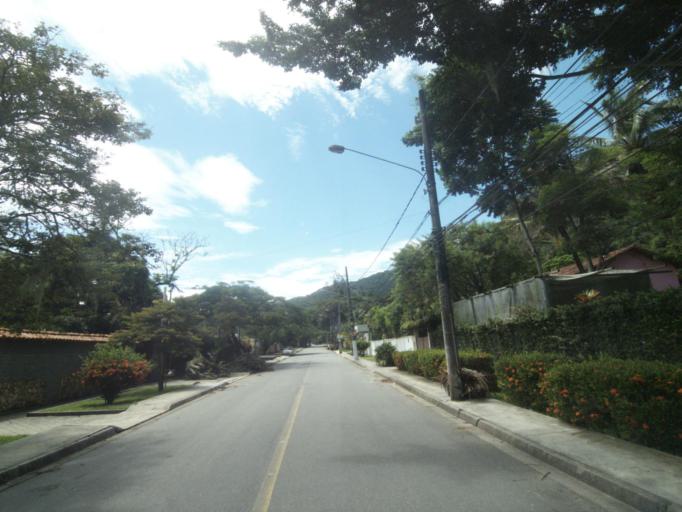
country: BR
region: Rio de Janeiro
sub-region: Niteroi
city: Niteroi
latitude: -22.9565
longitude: -43.0258
